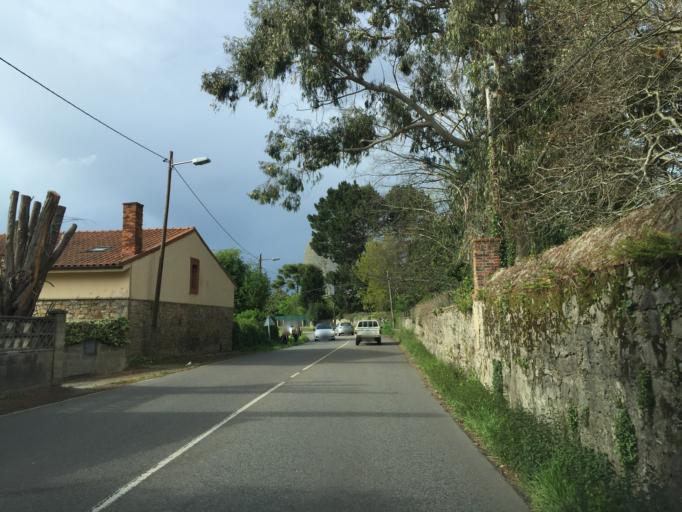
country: ES
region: Asturias
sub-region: Province of Asturias
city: Gijon
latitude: 43.5182
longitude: -5.6070
